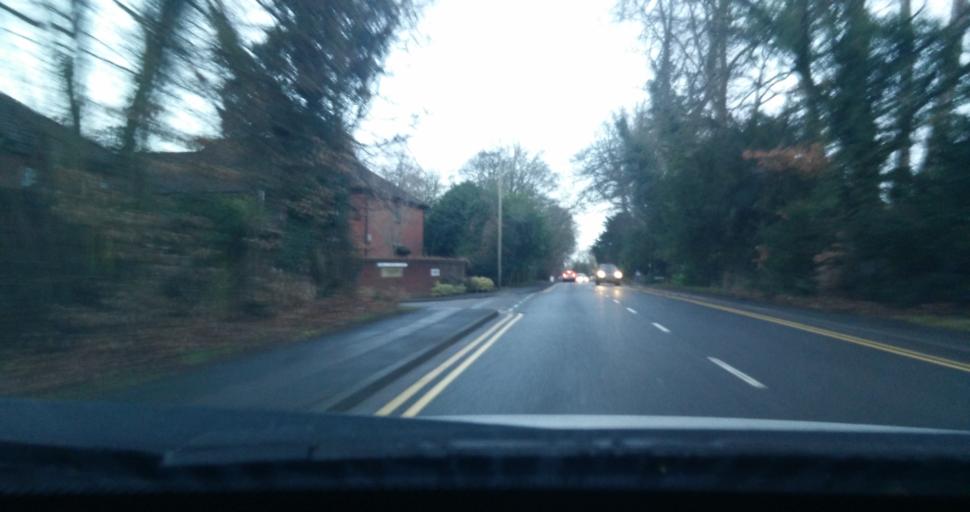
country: GB
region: England
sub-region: Buckinghamshire
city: Little Chalfont
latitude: 51.6648
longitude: -0.5672
